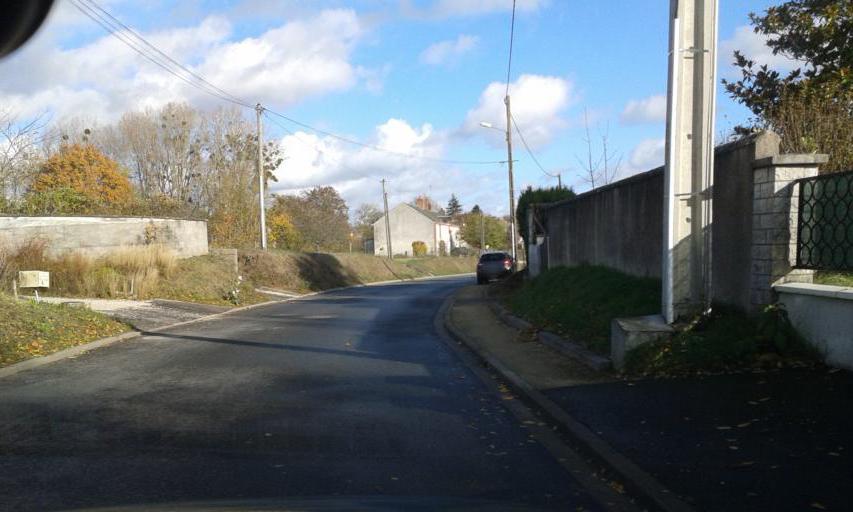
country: FR
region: Centre
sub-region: Departement du Loir-et-Cher
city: Saint-Laurent-Nouan
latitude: 47.7242
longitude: 1.5684
